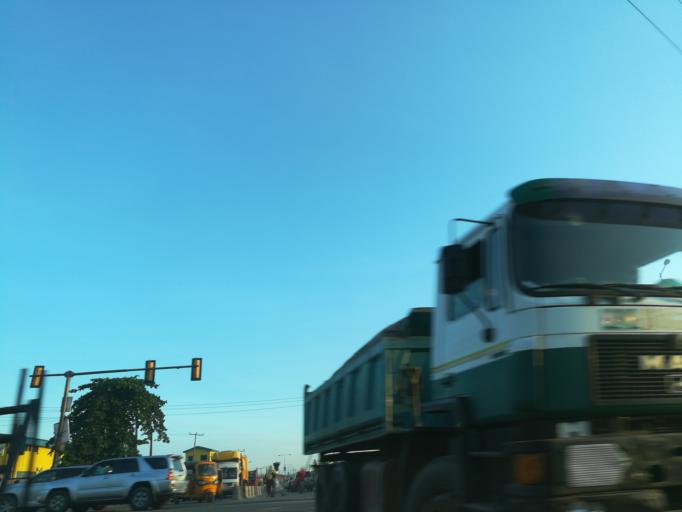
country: NG
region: Lagos
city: Ebute Ikorodu
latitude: 6.6196
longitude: 3.4753
